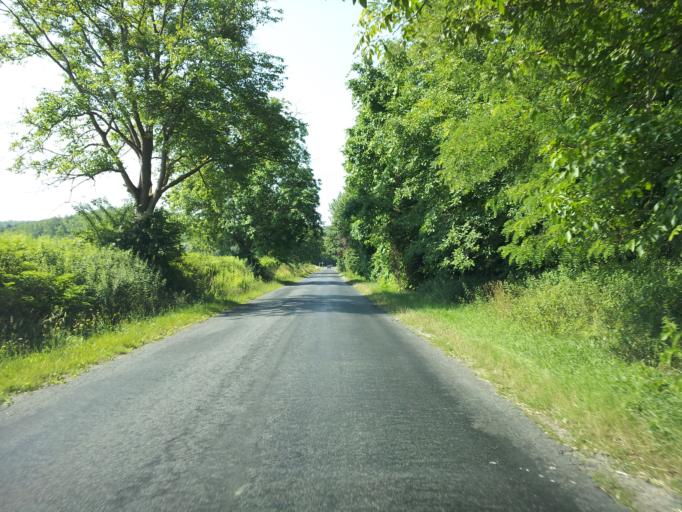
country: HU
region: Zala
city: Heviz
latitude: 46.8605
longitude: 17.1356
